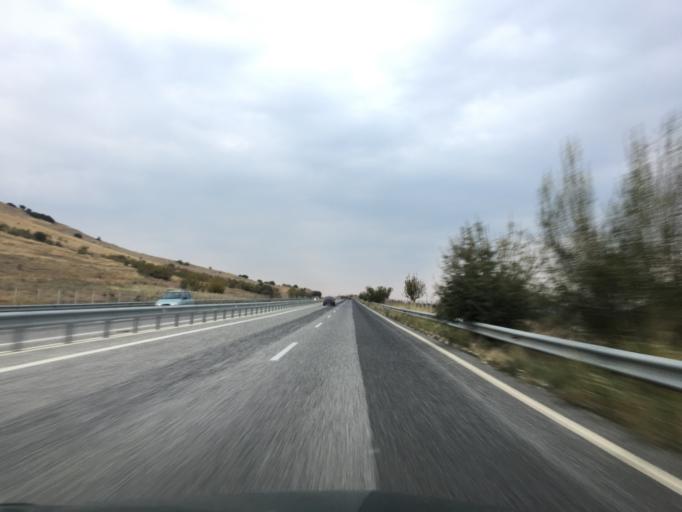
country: GR
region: Thessaly
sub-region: Trikala
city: Zarkos
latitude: 39.5977
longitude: 22.1959
